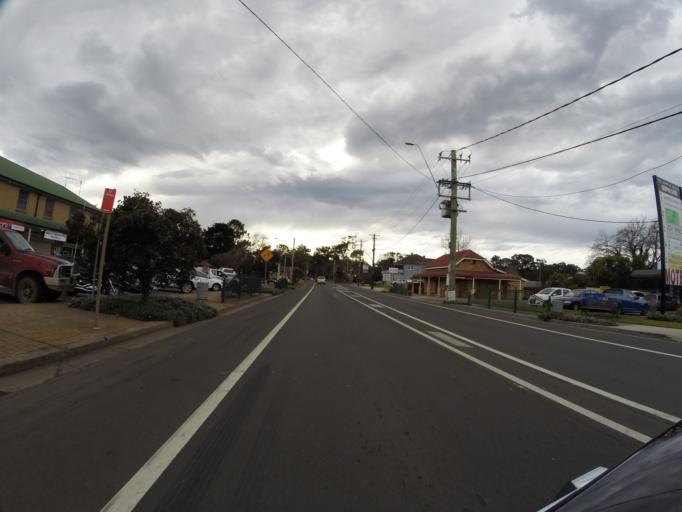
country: AU
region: New South Wales
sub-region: Wollondilly
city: Douglas Park
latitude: -34.2006
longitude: 150.7876
